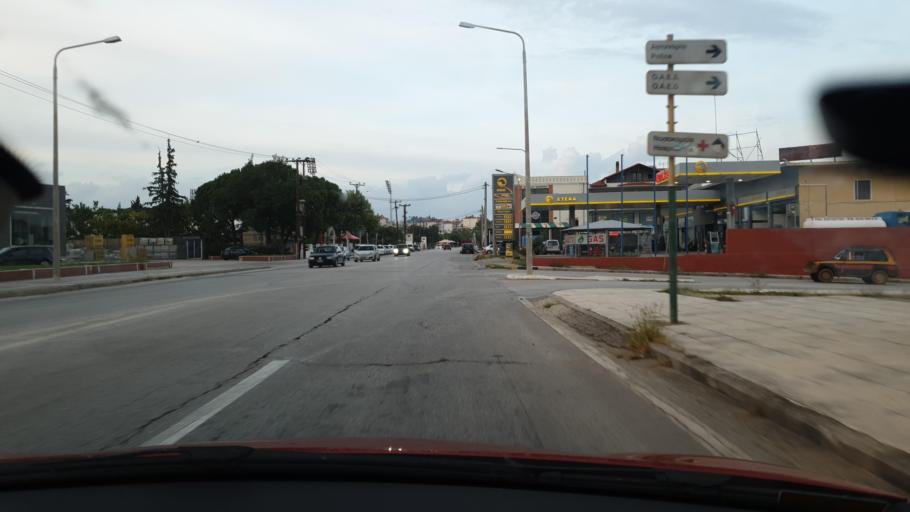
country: GR
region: Central Macedonia
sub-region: Nomos Kilkis
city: Kilkis
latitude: 40.9841
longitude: 22.8642
